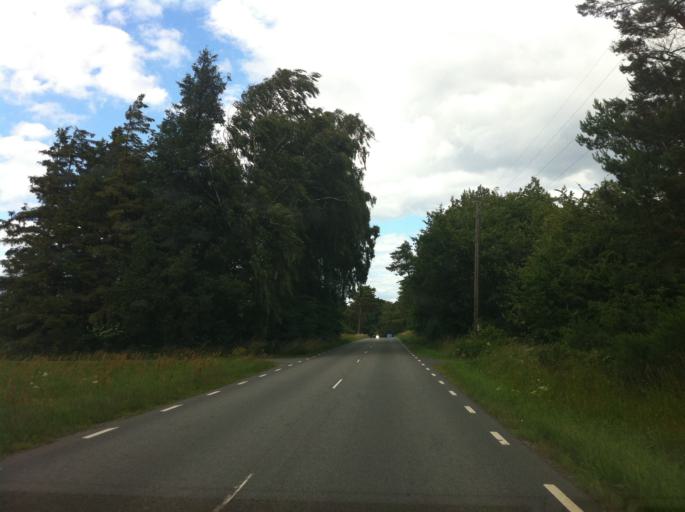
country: SE
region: Skane
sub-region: Simrishamns Kommun
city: Simrishamn
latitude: 55.4252
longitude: 14.2170
